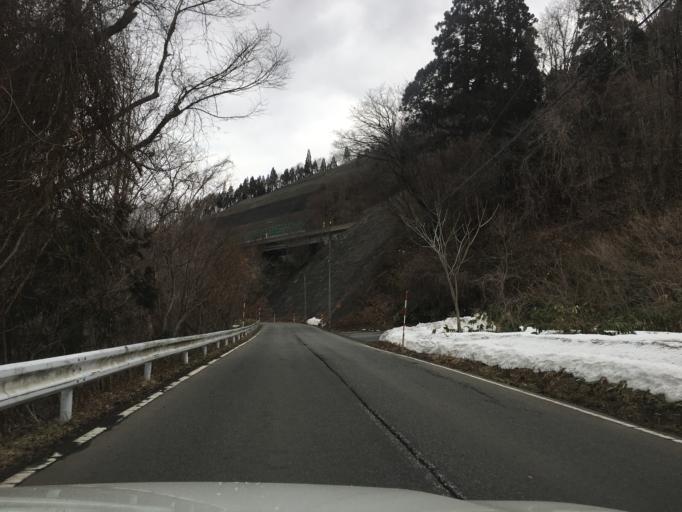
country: JP
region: Akita
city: Odate
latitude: 40.4268
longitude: 140.6531
